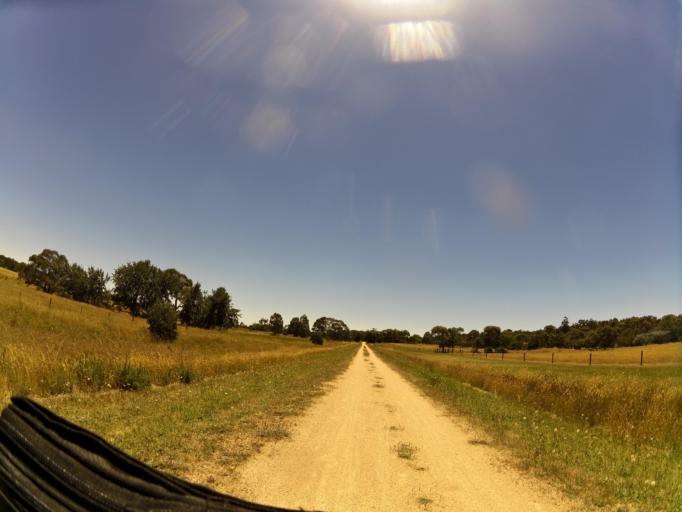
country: AU
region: Victoria
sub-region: Ballarat North
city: Delacombe
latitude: -37.6119
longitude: 143.7131
